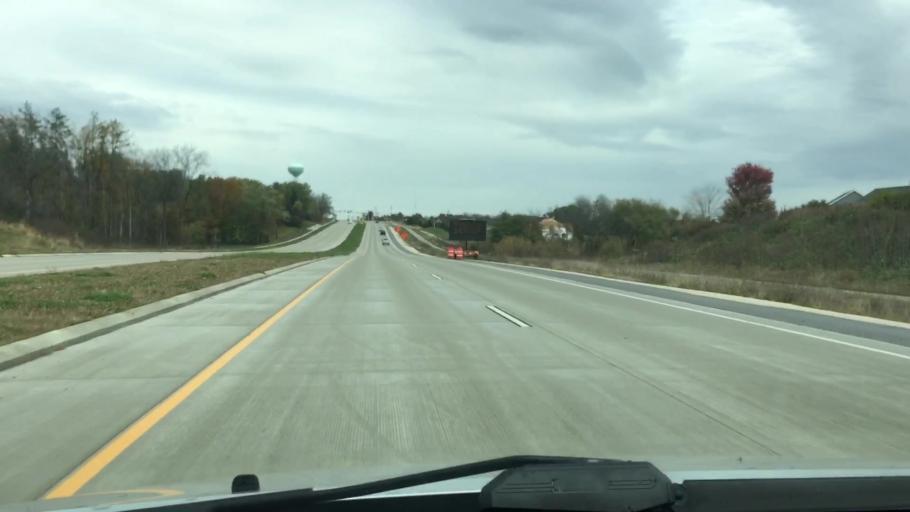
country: US
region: Wisconsin
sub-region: Waukesha County
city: Pewaukee
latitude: 43.0300
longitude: -88.2857
